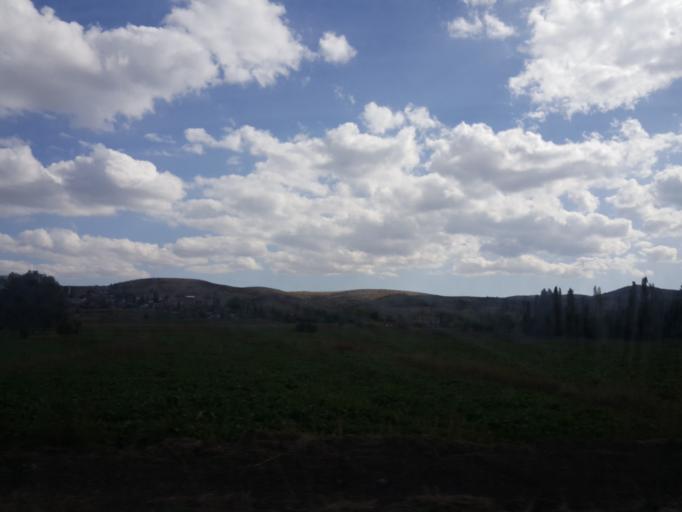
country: TR
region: Tokat
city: Yesilyurt
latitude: 40.0258
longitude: 36.2944
